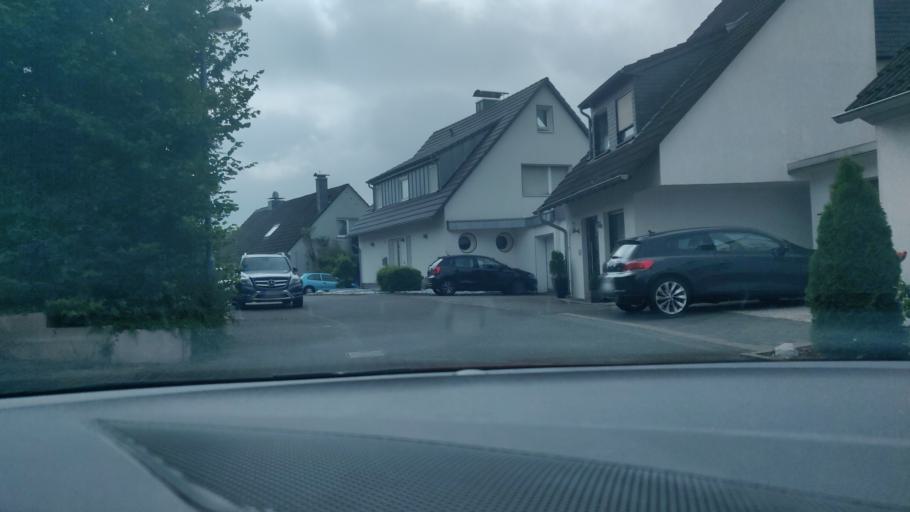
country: DE
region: North Rhine-Westphalia
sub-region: Regierungsbezirk Dusseldorf
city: Velbert
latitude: 51.3528
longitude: 7.0319
